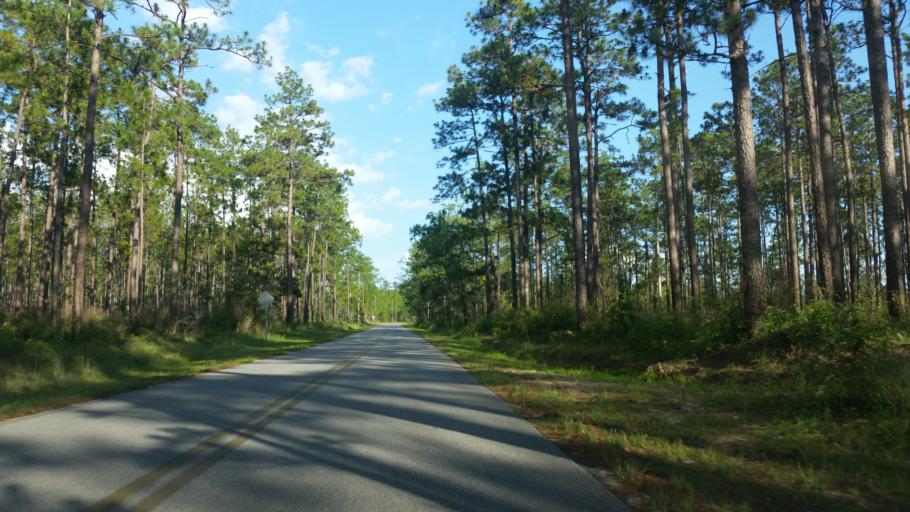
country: US
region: Florida
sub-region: Santa Rosa County
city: East Milton
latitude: 30.7017
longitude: -86.8787
